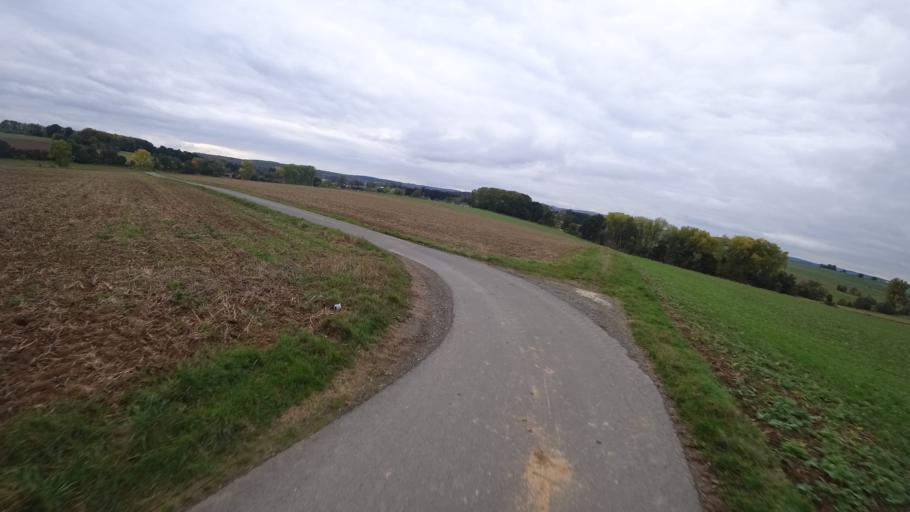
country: DE
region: Rheinland-Pfalz
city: Marienhausen
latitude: 50.5465
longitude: 7.6933
